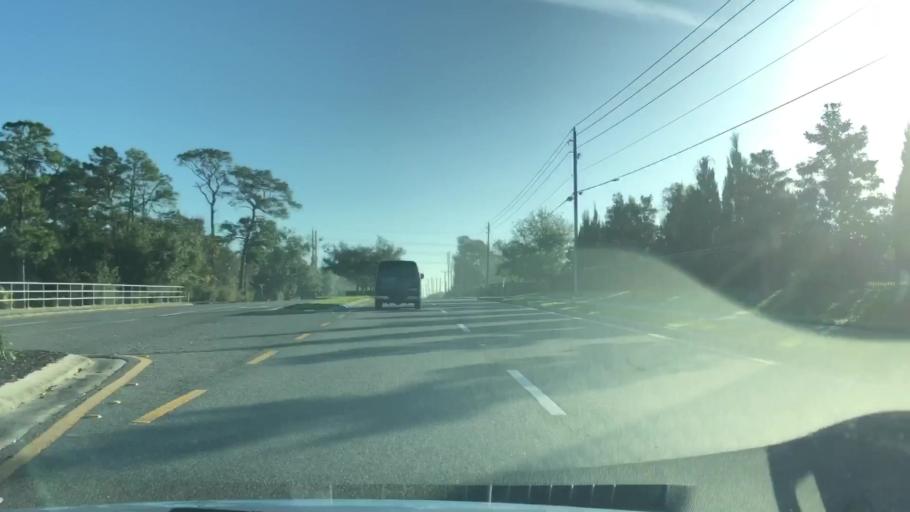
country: US
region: Florida
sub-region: Seminole County
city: Lake Mary
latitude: 28.7864
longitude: -81.3262
